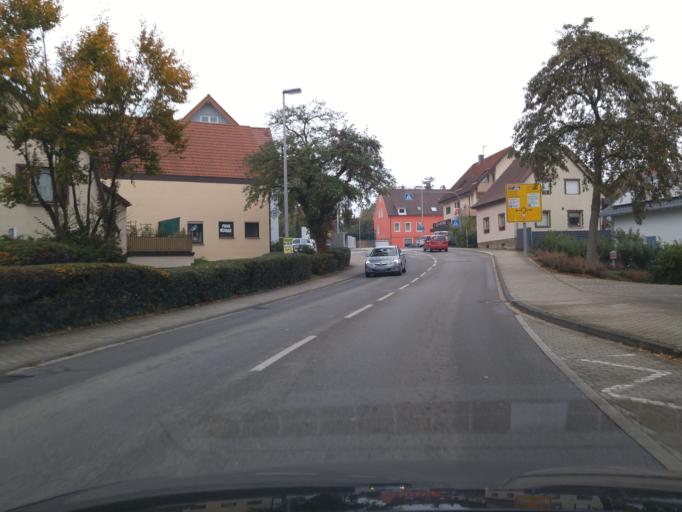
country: DE
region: Baden-Wuerttemberg
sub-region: Regierungsbezirk Stuttgart
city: Bad Rappenau
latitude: 49.2394
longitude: 9.1030
